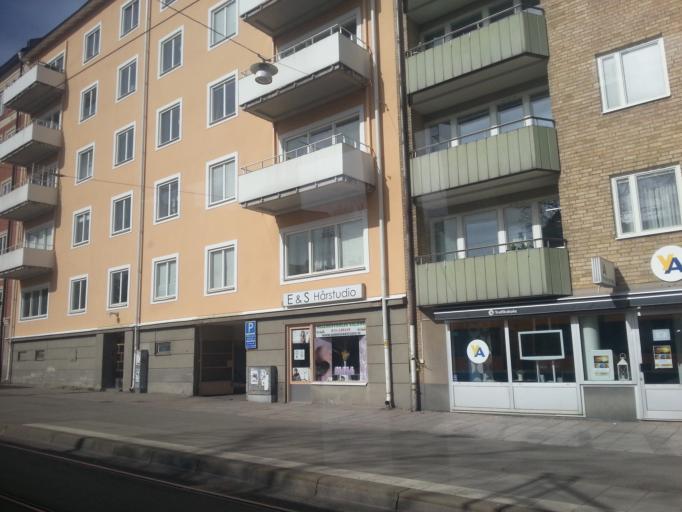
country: SE
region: OEstergoetland
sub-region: Norrkopings Kommun
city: Norrkoping
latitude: 58.5863
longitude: 16.1772
